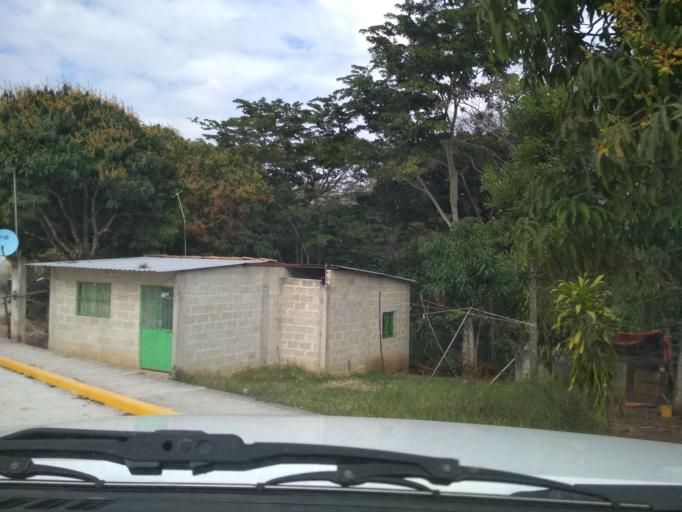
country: MX
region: Veracruz
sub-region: Coatepec
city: Tuzamapan
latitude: 19.3703
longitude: -96.8776
